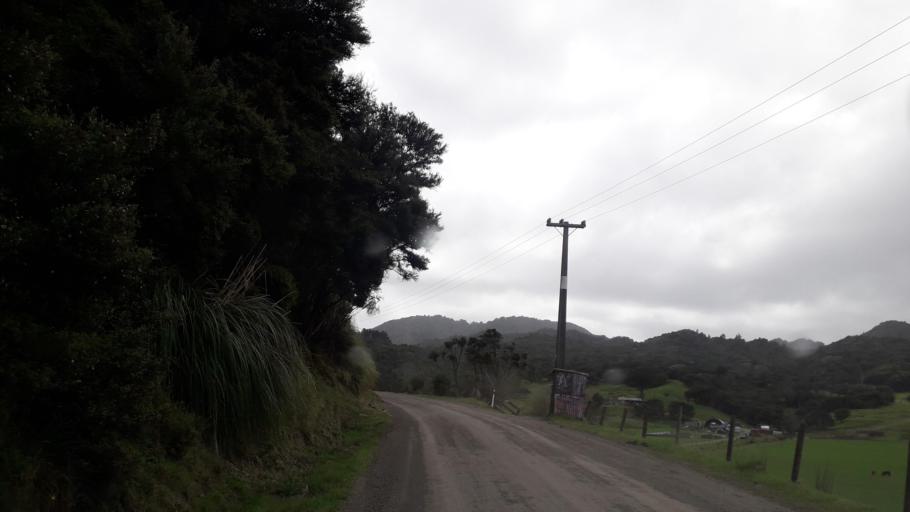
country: NZ
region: Northland
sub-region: Far North District
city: Ahipara
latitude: -35.4405
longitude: 173.3199
